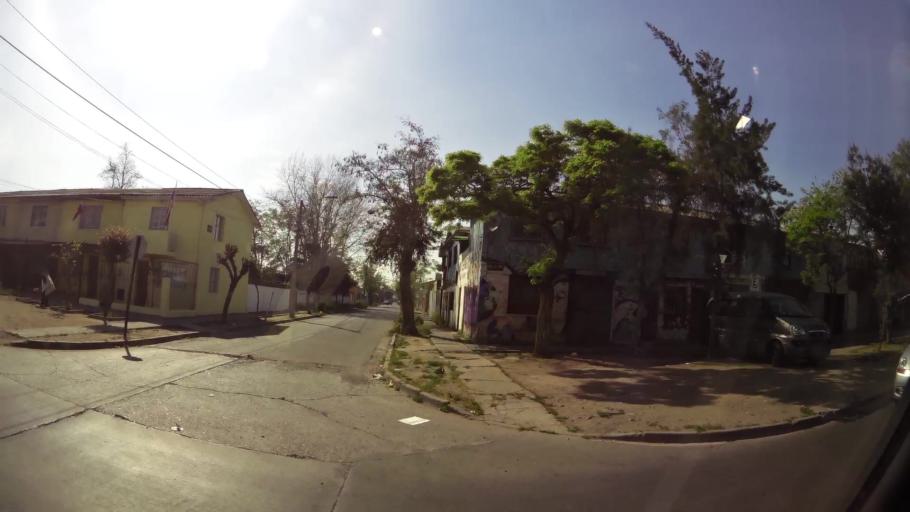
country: CL
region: Santiago Metropolitan
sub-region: Provincia de Santiago
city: Lo Prado
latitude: -33.4305
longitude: -70.7377
